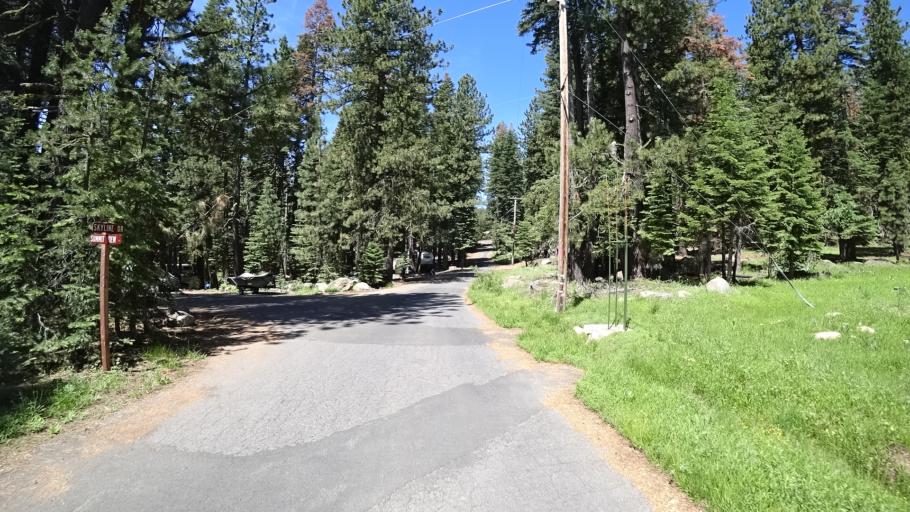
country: US
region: California
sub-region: Calaveras County
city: Arnold
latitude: 38.4262
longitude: -120.0990
